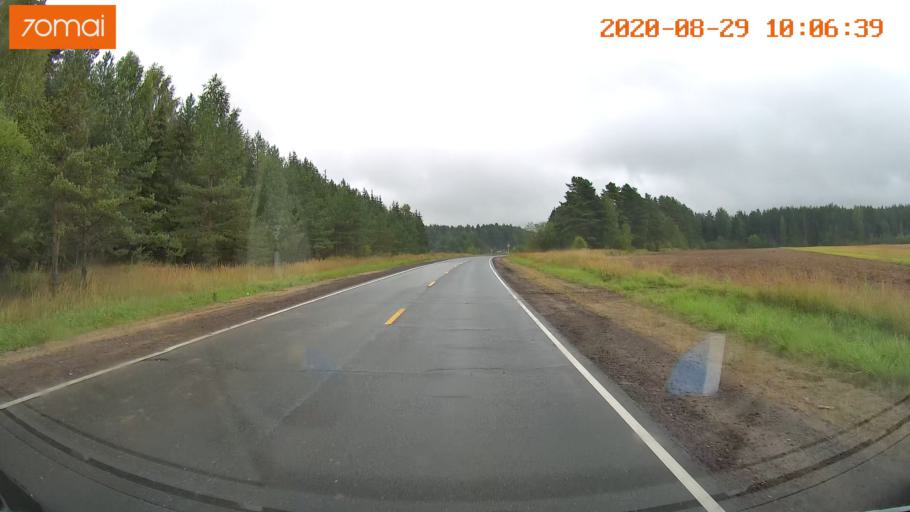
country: RU
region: Ivanovo
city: Kuznechikha
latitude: 57.3874
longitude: 42.5503
